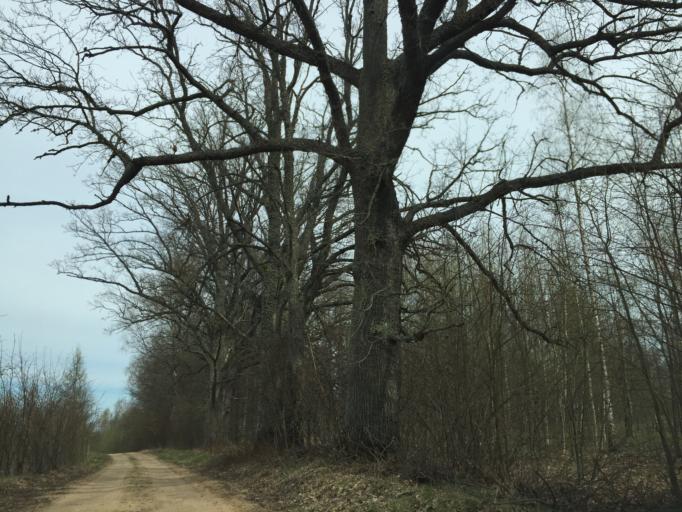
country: LV
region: Ludzas Rajons
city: Ludza
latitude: 56.5208
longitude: 27.5772
